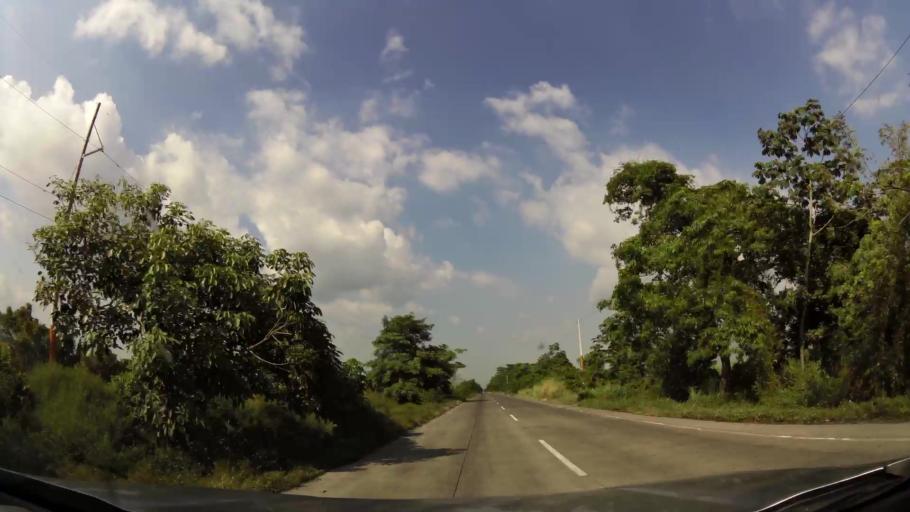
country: GT
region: Escuintla
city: Puerto San Jose
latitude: 14.0202
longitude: -90.7831
